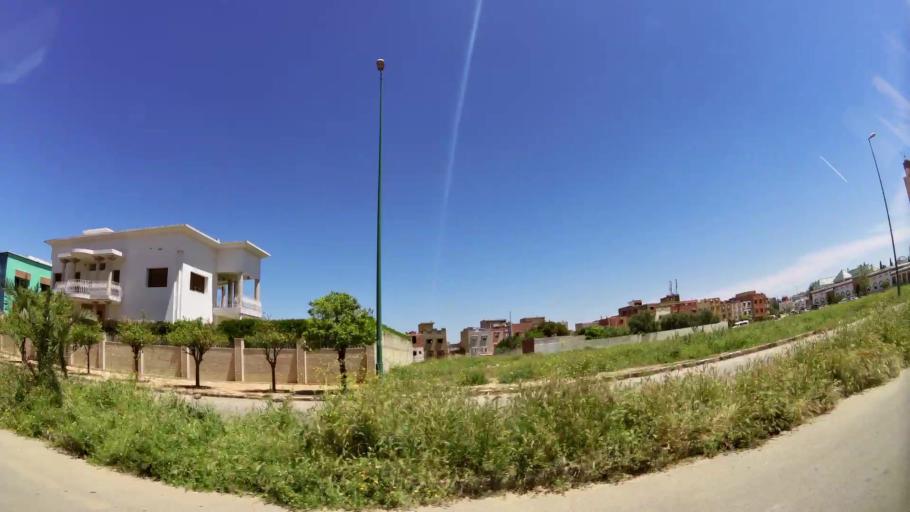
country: MA
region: Meknes-Tafilalet
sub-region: Meknes
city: Meknes
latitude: 33.9078
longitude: -5.5602
